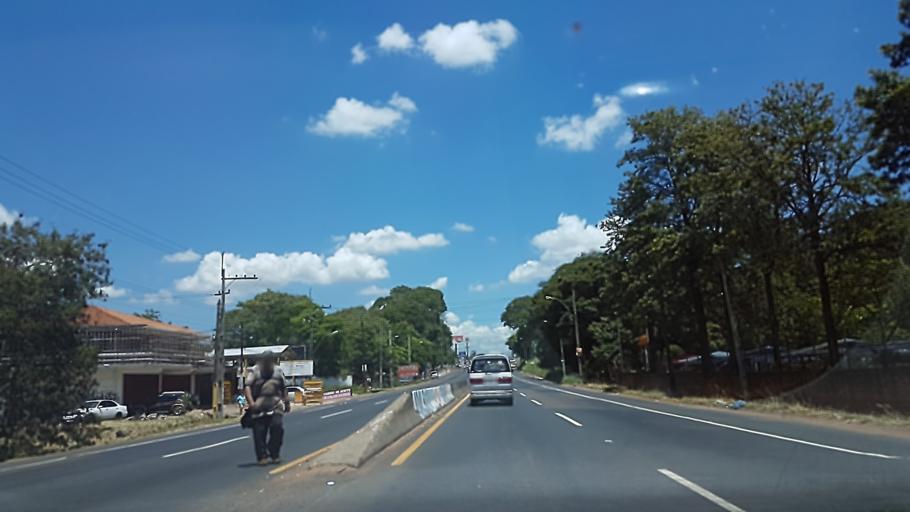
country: PY
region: Central
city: San Lorenzo
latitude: -25.3443
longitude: -57.4849
